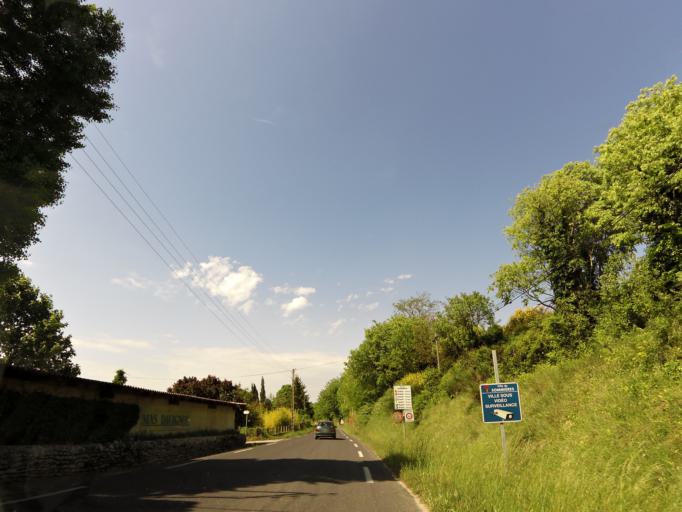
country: FR
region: Languedoc-Roussillon
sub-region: Departement du Gard
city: Sommieres
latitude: 43.7705
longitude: 4.0924
